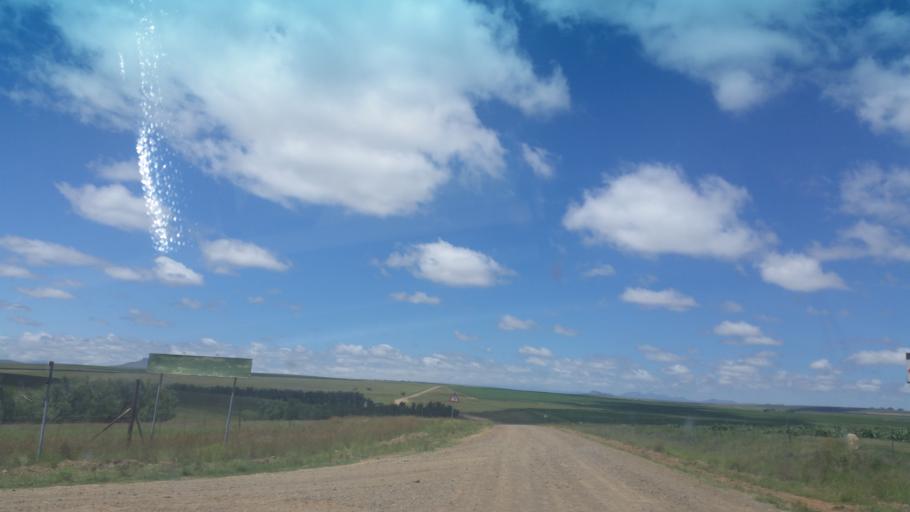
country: ZA
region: Orange Free State
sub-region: Thabo Mofutsanyana District Municipality
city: Harrismith
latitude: -28.2168
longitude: 28.9686
